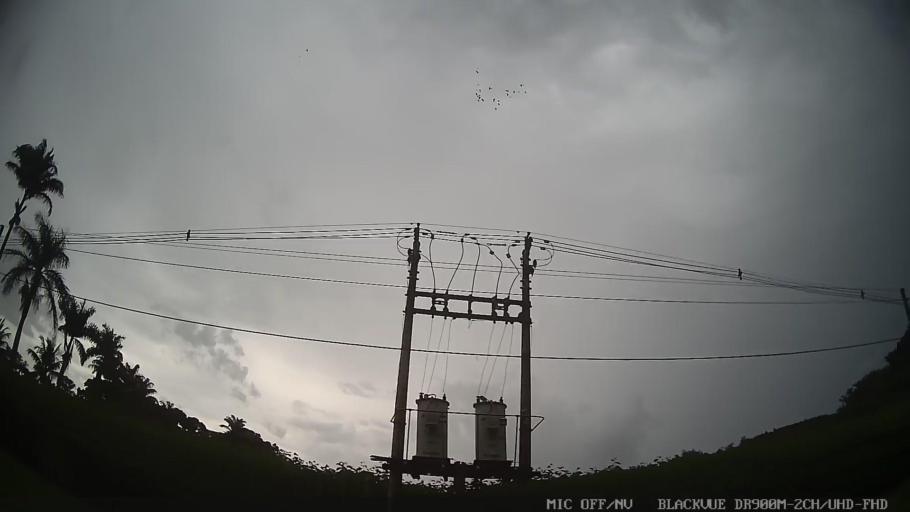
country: BR
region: Sao Paulo
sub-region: Pedreira
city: Pedreira
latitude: -22.7170
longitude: -46.8581
